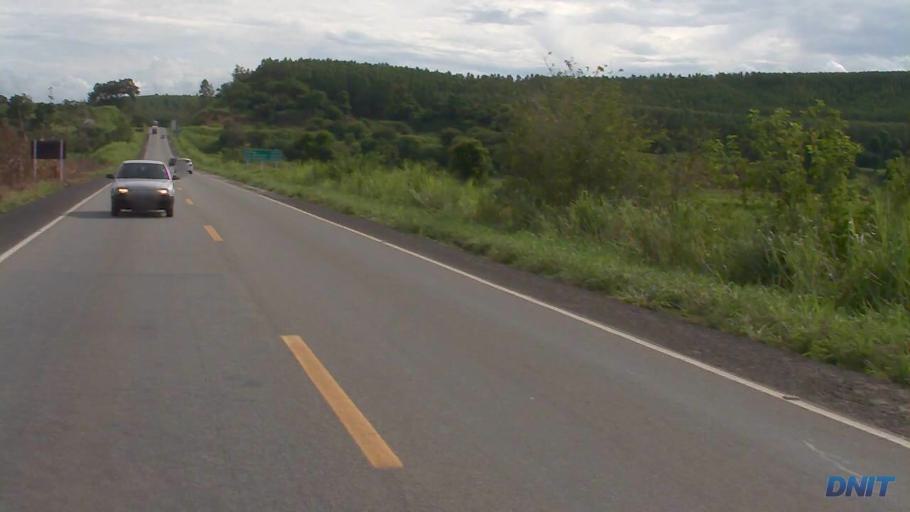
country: BR
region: Minas Gerais
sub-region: Belo Oriente
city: Belo Oriente
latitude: -19.2415
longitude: -42.3348
